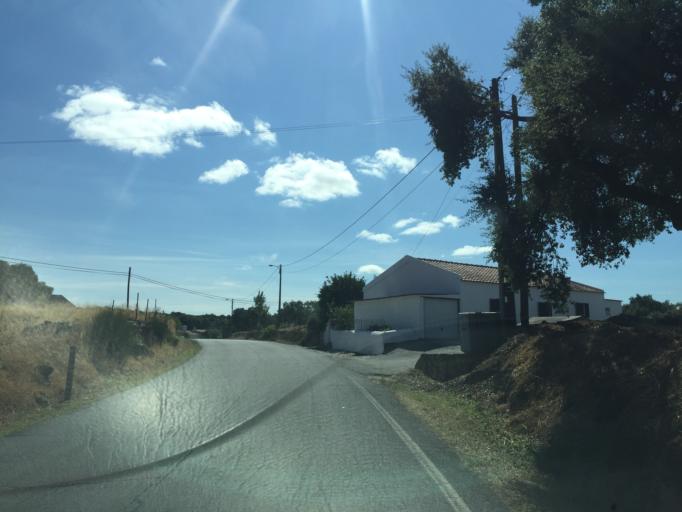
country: PT
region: Portalegre
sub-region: Marvao
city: Marvao
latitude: 39.4404
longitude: -7.3667
